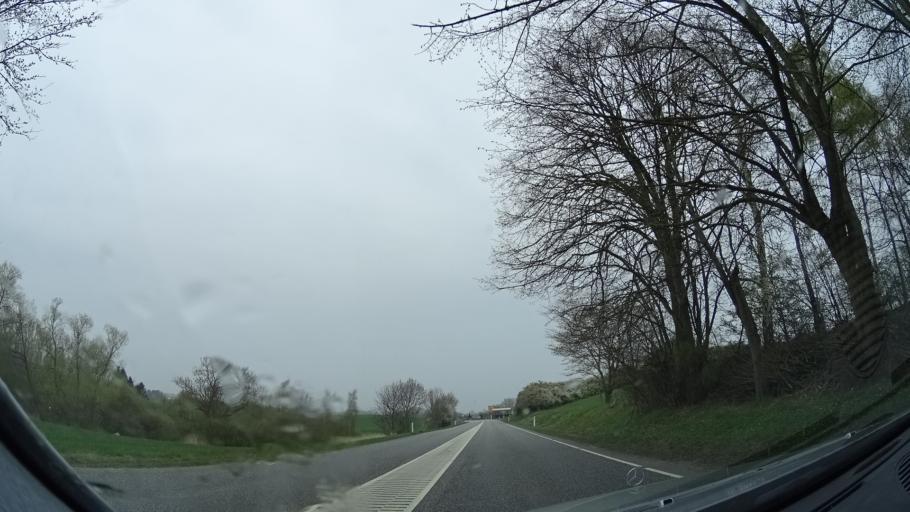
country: DK
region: Zealand
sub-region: Odsherred Kommune
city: Asnaes
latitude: 55.7929
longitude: 11.6002
